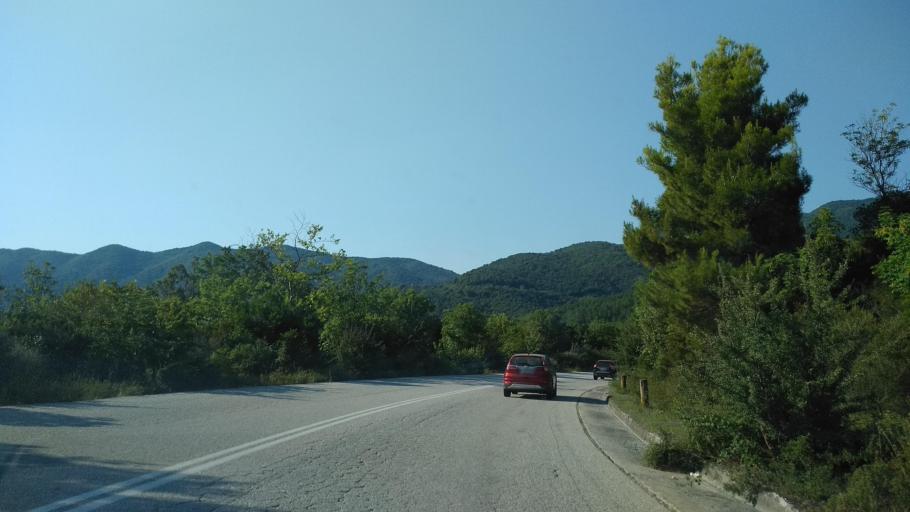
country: GR
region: Central Macedonia
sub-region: Nomos Chalkidikis
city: Stratonion
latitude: 40.5601
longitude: 23.8243
